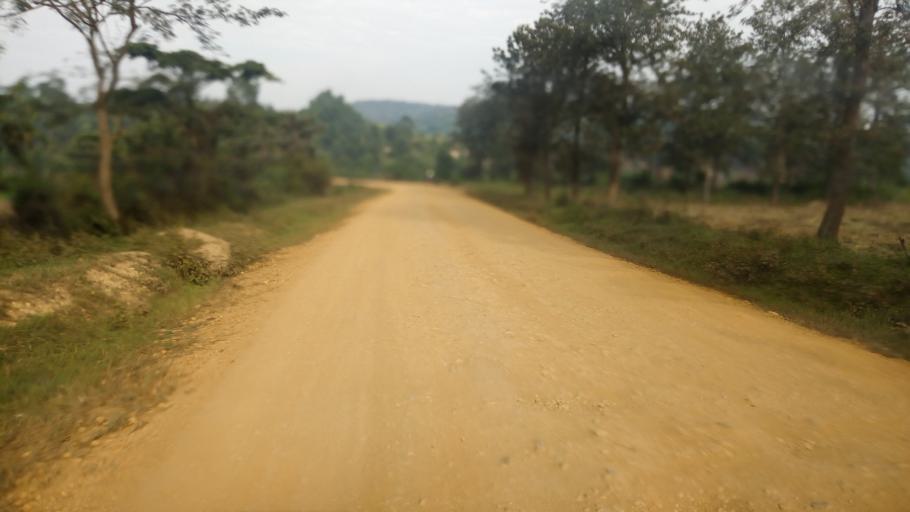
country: UG
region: Western Region
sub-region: Kanungu District
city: Ntungamo
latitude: -0.8388
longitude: 29.6426
